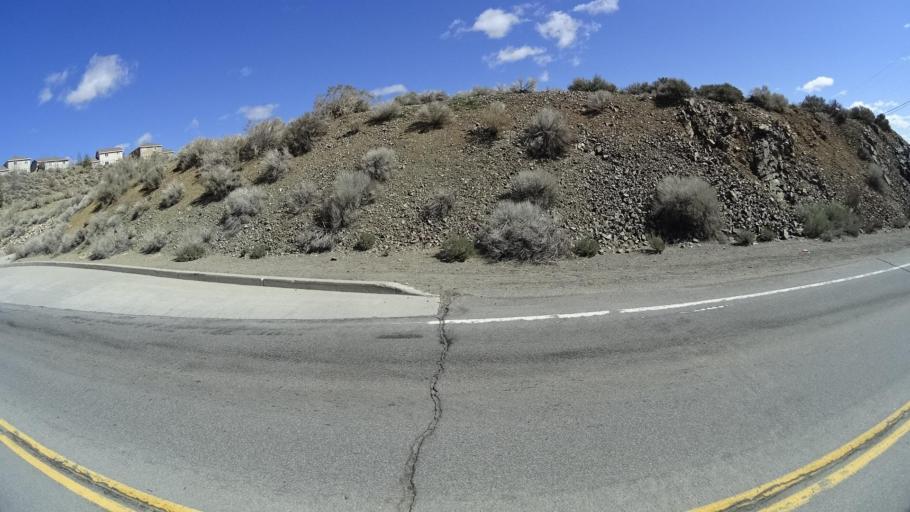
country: US
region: Nevada
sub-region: Washoe County
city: Golden Valley
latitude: 39.5855
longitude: -119.8309
